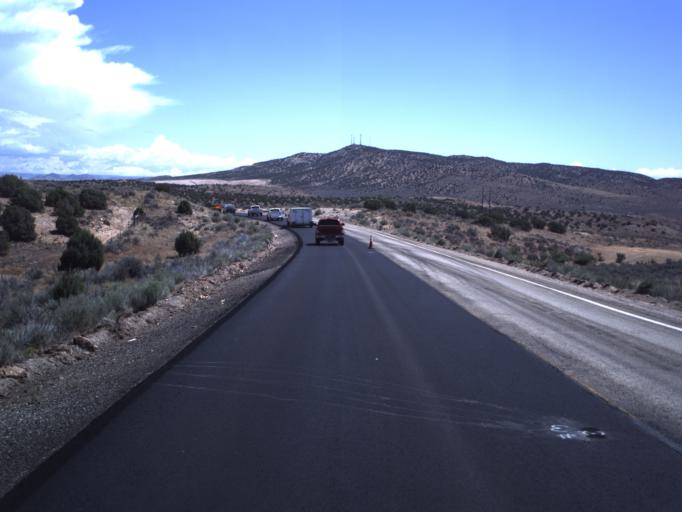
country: US
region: Utah
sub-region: Uintah County
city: Maeser
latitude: 40.4304
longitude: -109.6590
